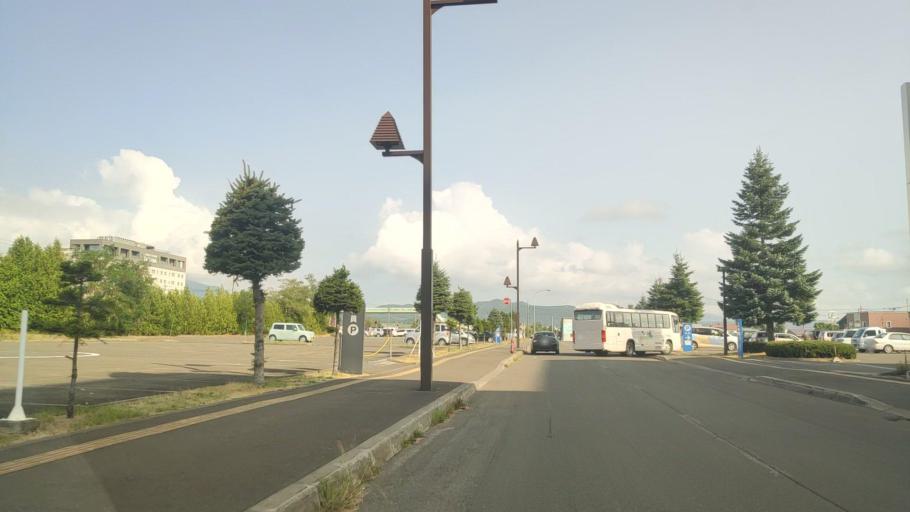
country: JP
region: Hokkaido
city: Shimo-furano
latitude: 43.3477
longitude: 142.3921
